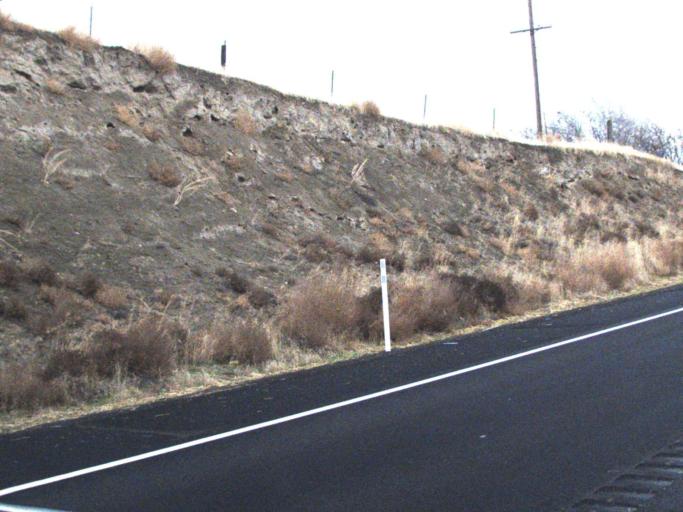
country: US
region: Washington
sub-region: Walla Walla County
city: Garrett
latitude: 46.0493
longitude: -118.7029
